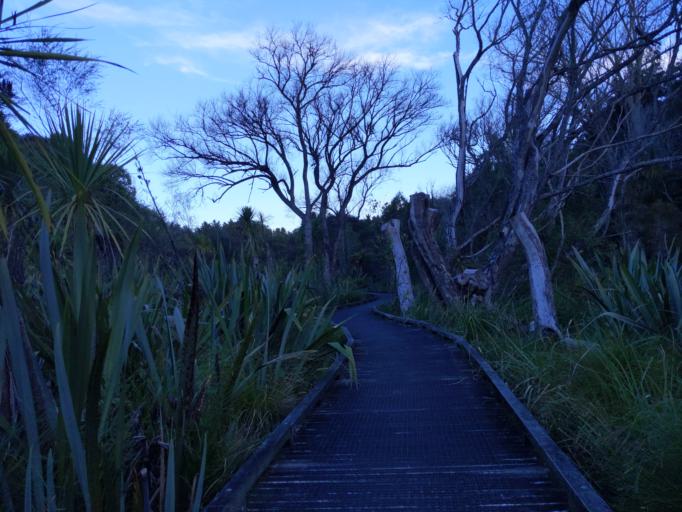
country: NZ
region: Waikato
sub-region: Hamilton City
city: Hamilton
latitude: -37.7429
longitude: 175.2756
